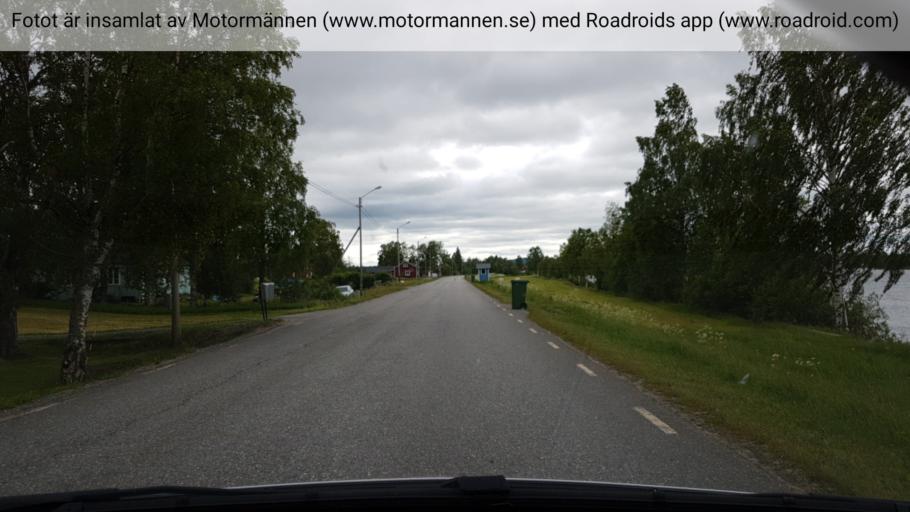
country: SE
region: Vaesterbotten
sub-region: Vannas Kommun
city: Vannasby
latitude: 63.9486
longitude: 19.8734
